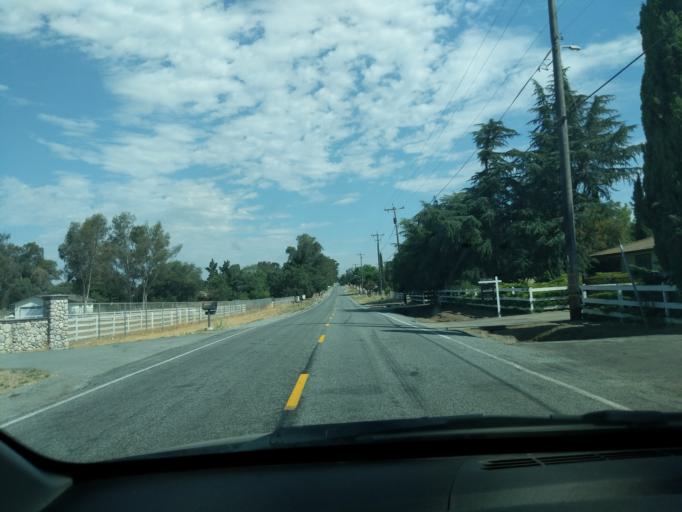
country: US
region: California
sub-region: Santa Clara County
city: San Martin
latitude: 37.0650
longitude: -121.5548
